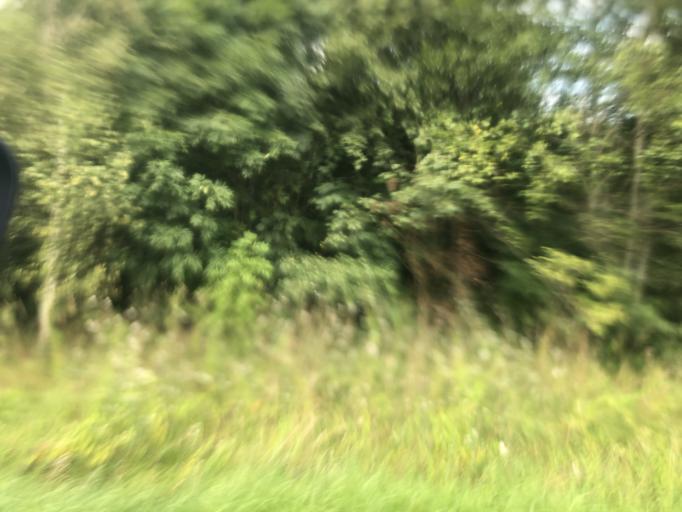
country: LV
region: Vecumnieki
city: Vecumnieki
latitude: 56.4666
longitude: 24.6691
